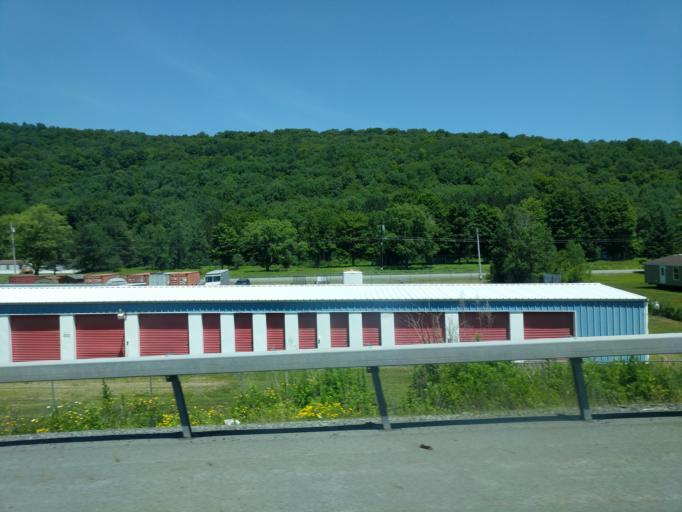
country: US
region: New York
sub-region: Sullivan County
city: Livingston Manor
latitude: 41.8642
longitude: -74.7879
